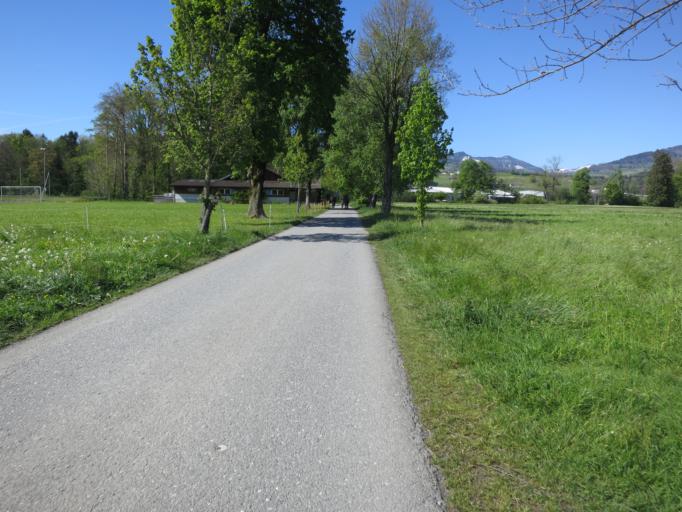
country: CH
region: Saint Gallen
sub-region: Wahlkreis See-Gaster
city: Schmerikon
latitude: 47.2204
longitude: 8.9558
